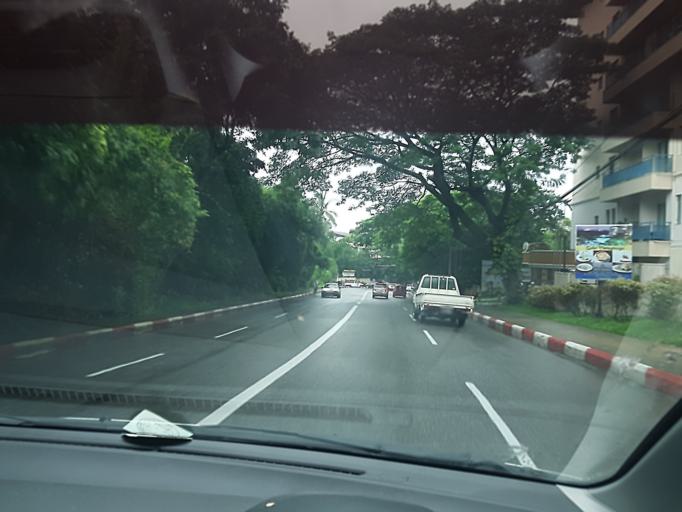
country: MM
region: Yangon
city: Yangon
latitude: 16.8122
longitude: 96.1418
